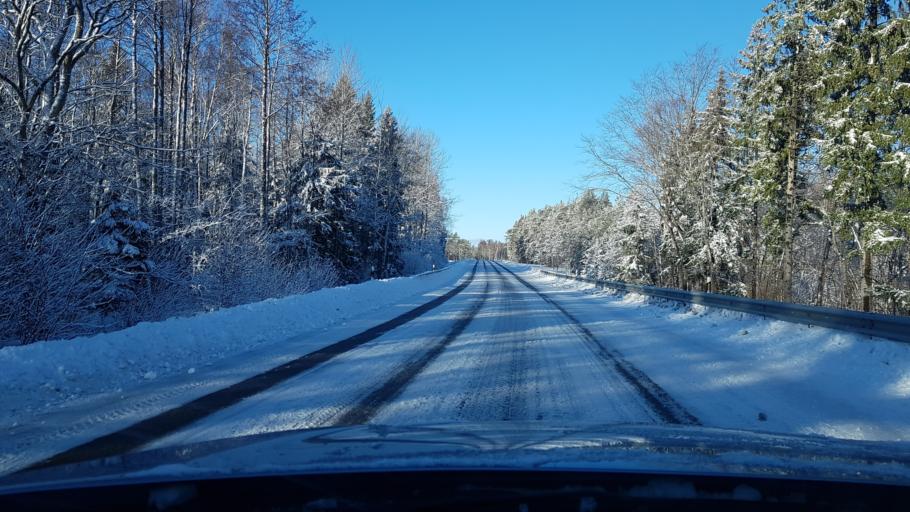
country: EE
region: Hiiumaa
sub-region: Kaerdla linn
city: Kardla
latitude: 58.9671
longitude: 22.7724
